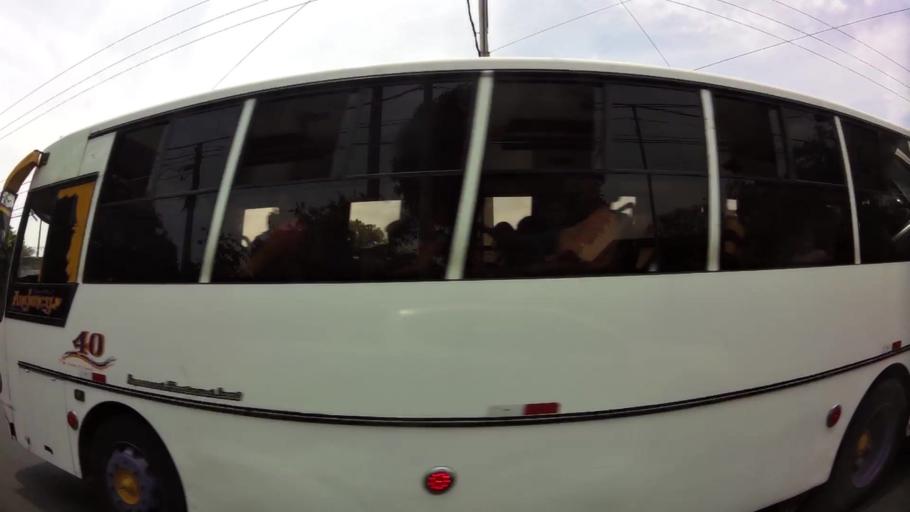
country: NI
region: Managua
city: Managua
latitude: 12.1552
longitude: -86.2938
